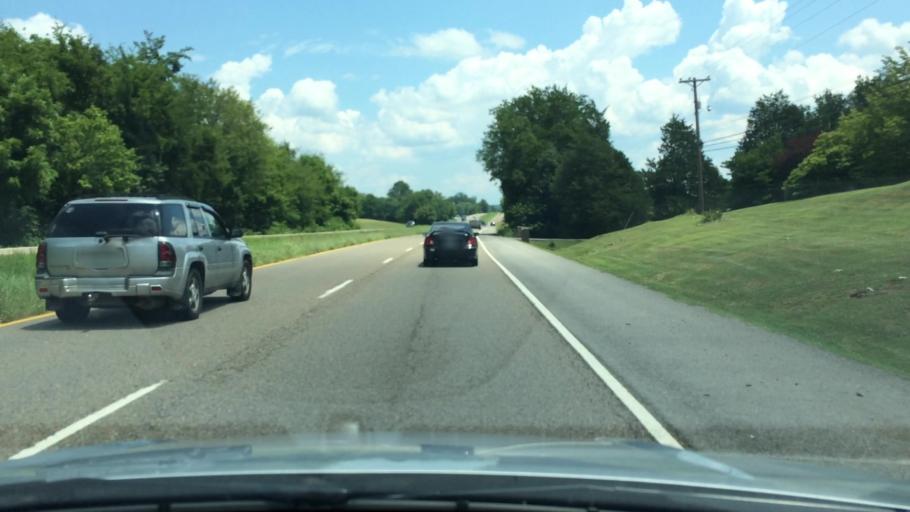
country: US
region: Tennessee
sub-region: Knox County
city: Mascot
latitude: 36.0675
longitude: -83.6672
